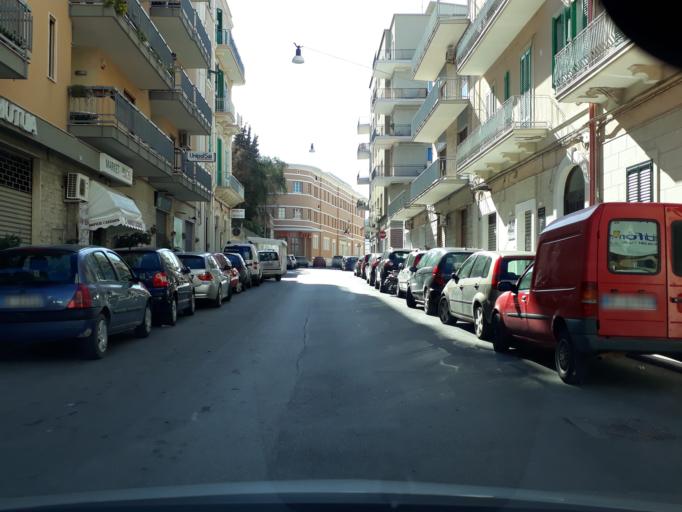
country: IT
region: Apulia
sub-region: Provincia di Bari
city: Monopoli
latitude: 40.9519
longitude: 17.2961
